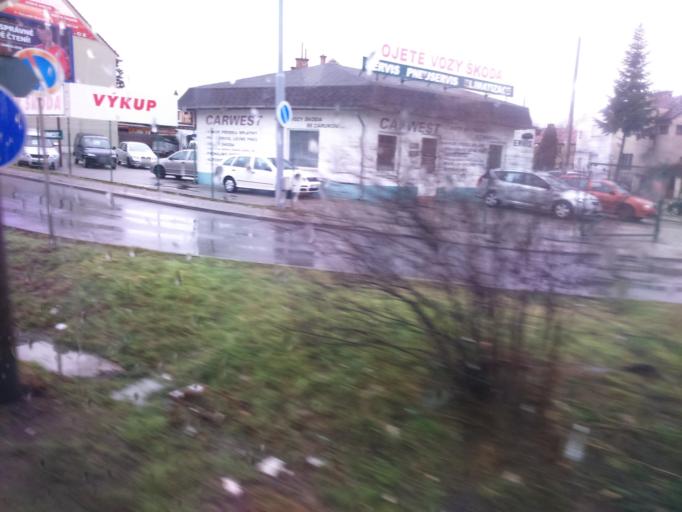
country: CZ
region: Plzensky
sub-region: Okres Plzen-Mesto
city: Pilsen
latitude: 49.7367
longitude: 13.3320
